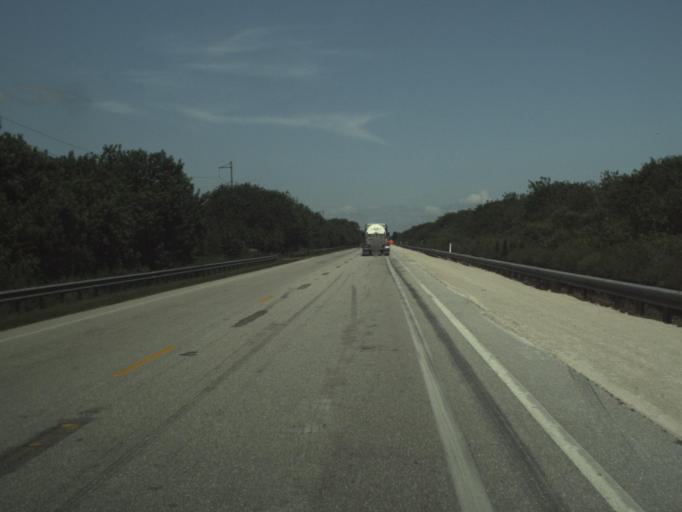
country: US
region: Florida
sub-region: Okeechobee County
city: Taylor Creek
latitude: 27.1375
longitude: -80.6448
